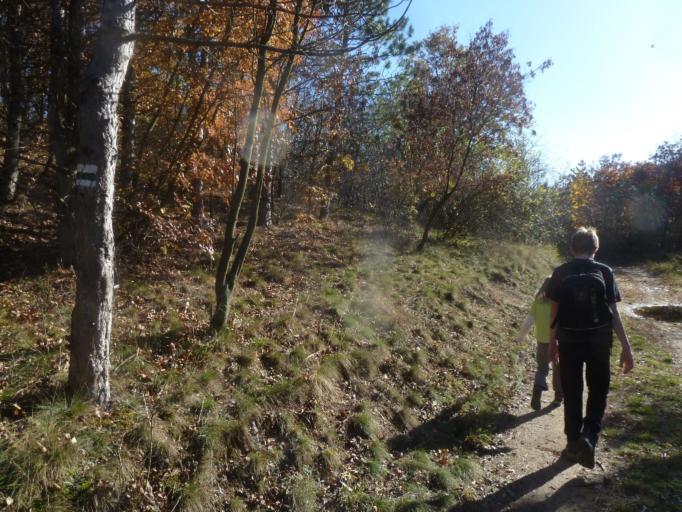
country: HU
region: Fejer
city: Pakozd
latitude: 47.2260
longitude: 18.5315
